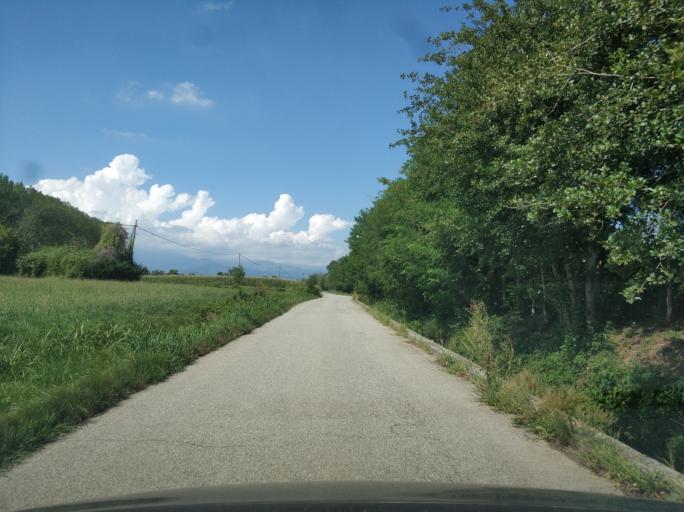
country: IT
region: Piedmont
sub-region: Provincia di Torino
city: Feletto
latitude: 45.3036
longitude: 7.7239
